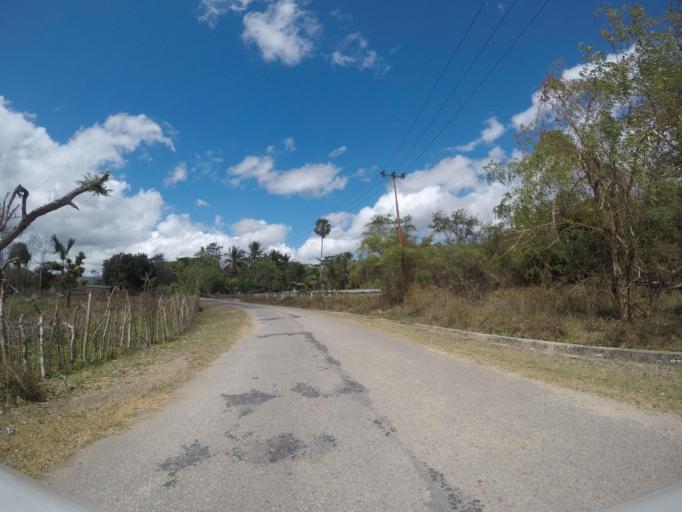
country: TL
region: Lautem
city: Lospalos
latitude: -8.4691
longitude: 126.8175
